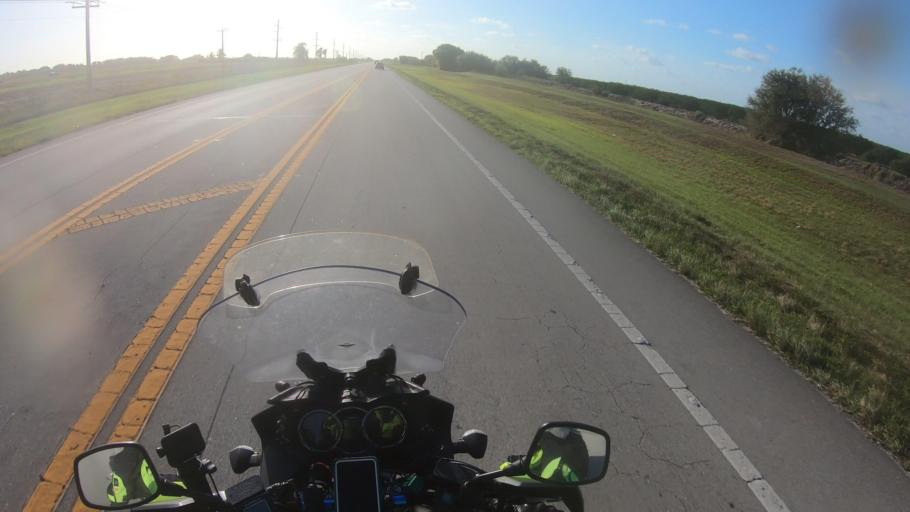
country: US
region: Florida
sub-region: DeSoto County
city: Southeast Arcadia
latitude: 27.2104
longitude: -81.6896
